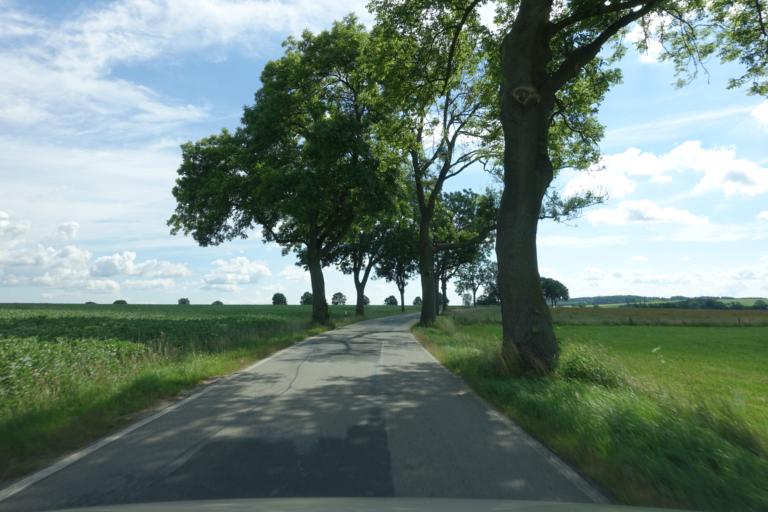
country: DE
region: Saxony
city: Frankenstein
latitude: 50.8572
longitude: 13.2290
